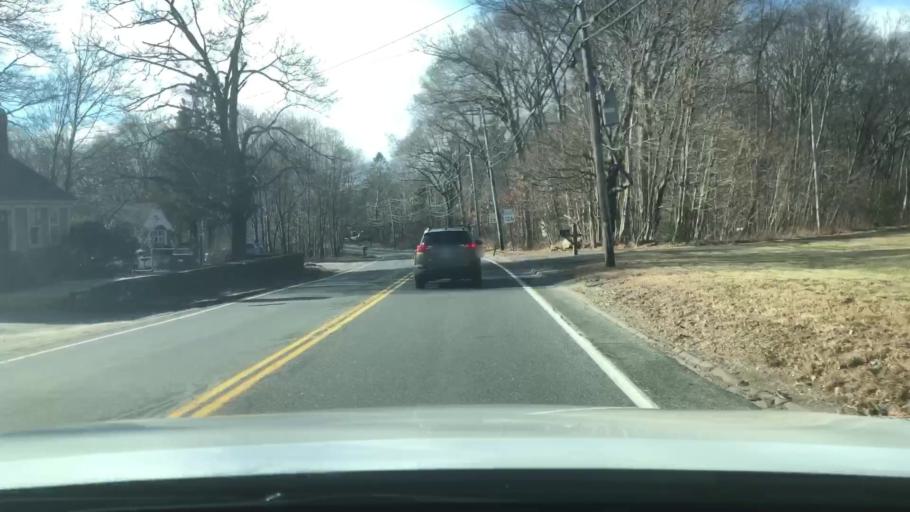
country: US
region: Rhode Island
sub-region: Providence County
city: Woonsocket
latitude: 42.0400
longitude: -71.4899
